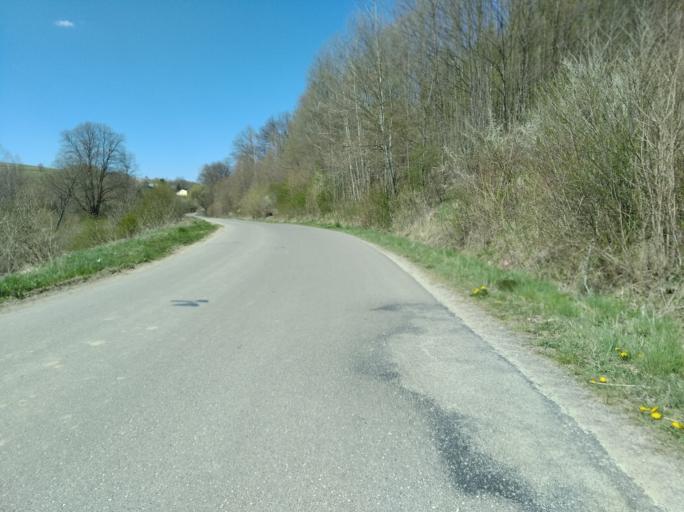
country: PL
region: Subcarpathian Voivodeship
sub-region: Powiat brzozowski
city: Dydnia
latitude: 49.7065
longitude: 22.1486
